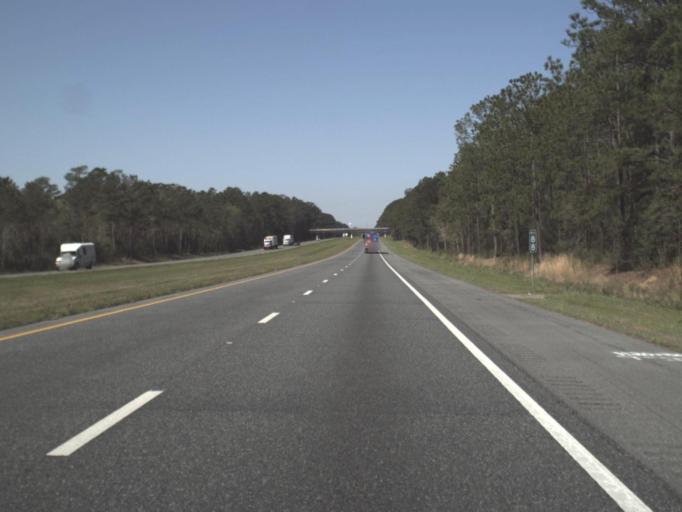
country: US
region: Florida
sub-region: Walton County
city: DeFuniak Springs
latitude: 30.6911
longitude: -86.0647
